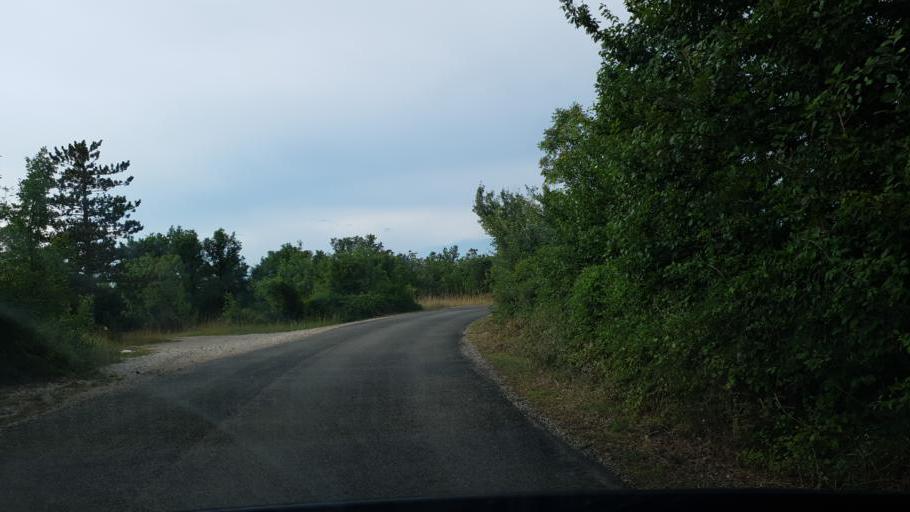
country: HR
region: Primorsko-Goranska
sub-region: Grad Crikvenica
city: Jadranovo
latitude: 45.1725
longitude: 14.6058
